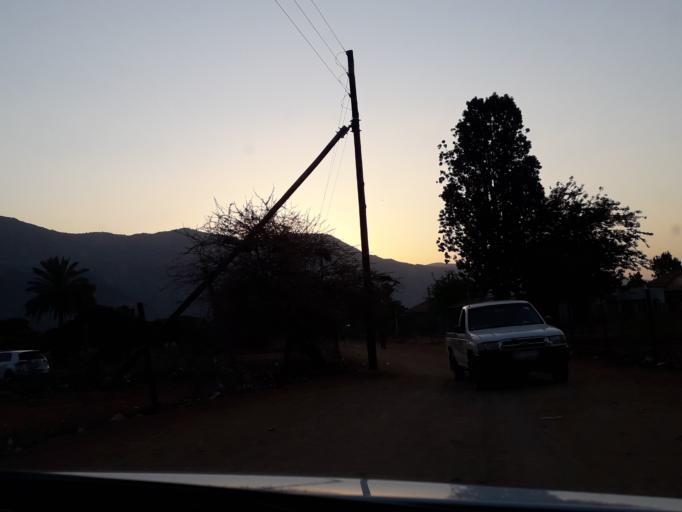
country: ZA
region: Limpopo
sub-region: Waterberg District Municipality
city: Mokopane
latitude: -24.1568
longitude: 28.9499
